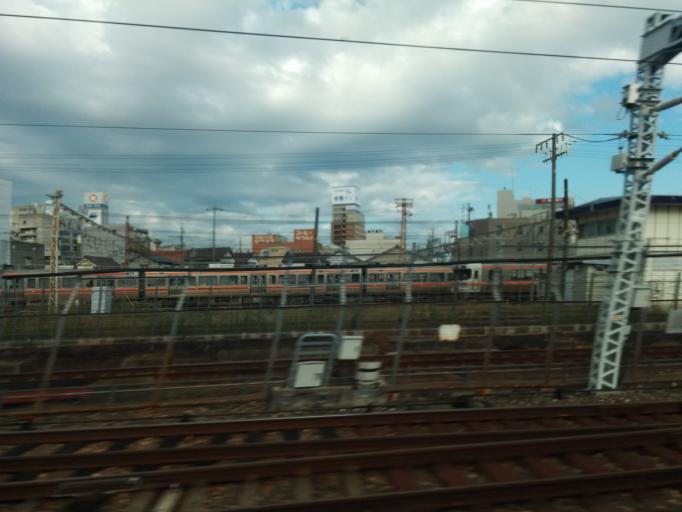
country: JP
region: Aichi
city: Toyohashi
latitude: 34.7657
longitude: 137.3798
